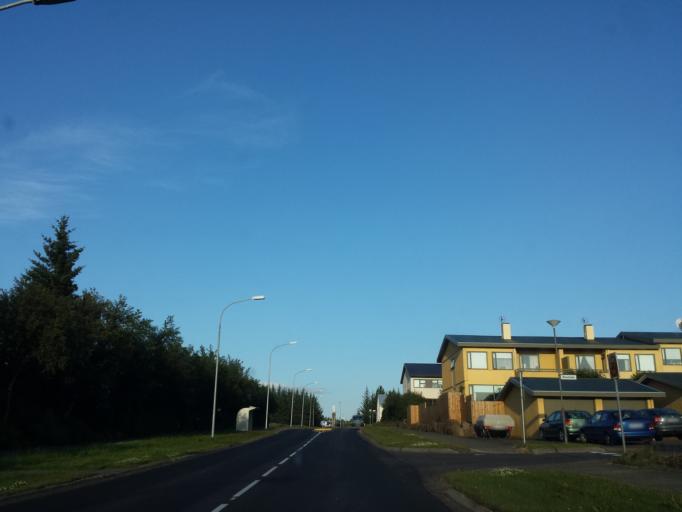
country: IS
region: Capital Region
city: Mosfellsbaer
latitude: 64.1150
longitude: -21.7890
